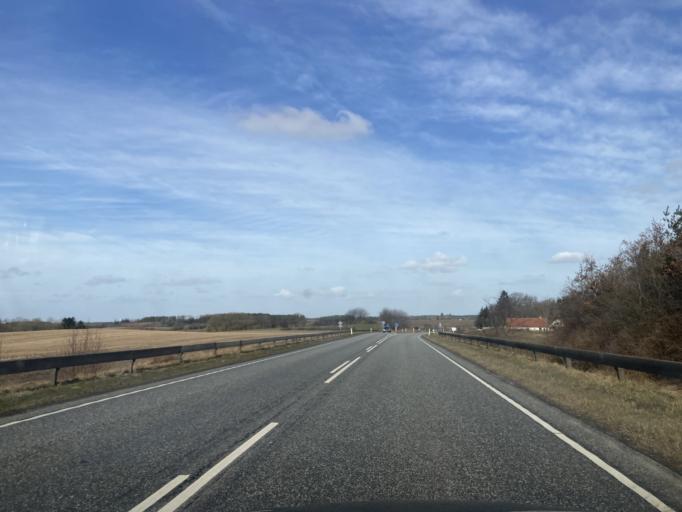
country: DK
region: Central Jutland
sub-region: Hedensted Kommune
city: Torring
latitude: 55.9876
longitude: 9.3902
